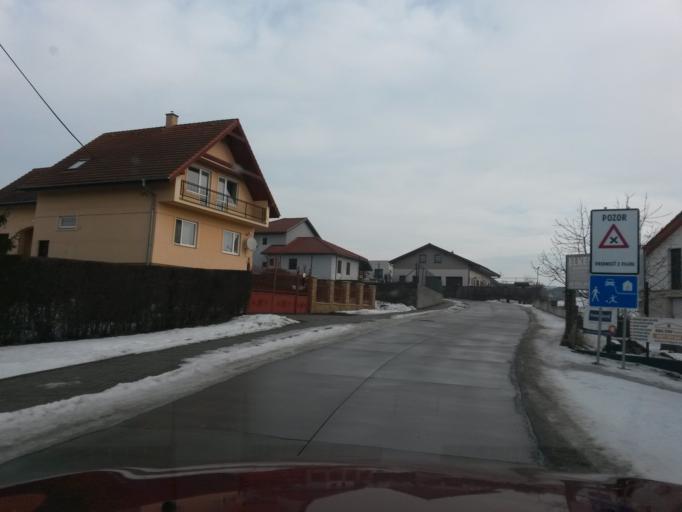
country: SK
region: Kosicky
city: Kosice
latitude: 48.7824
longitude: 21.3251
